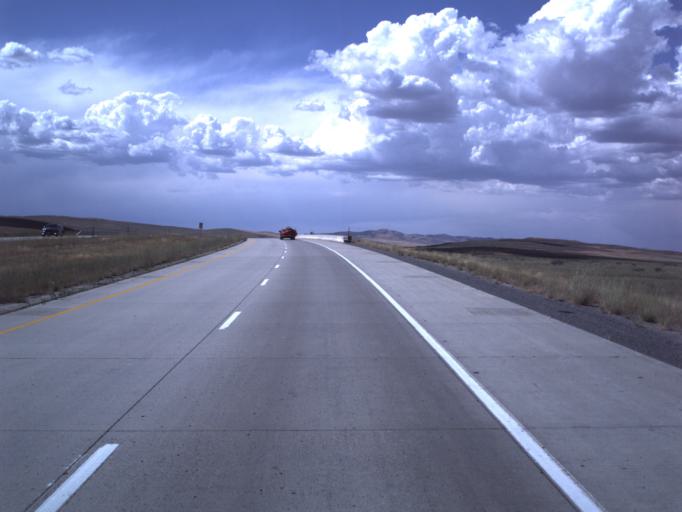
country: US
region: Utah
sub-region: Box Elder County
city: Garland
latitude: 41.8716
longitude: -112.4647
